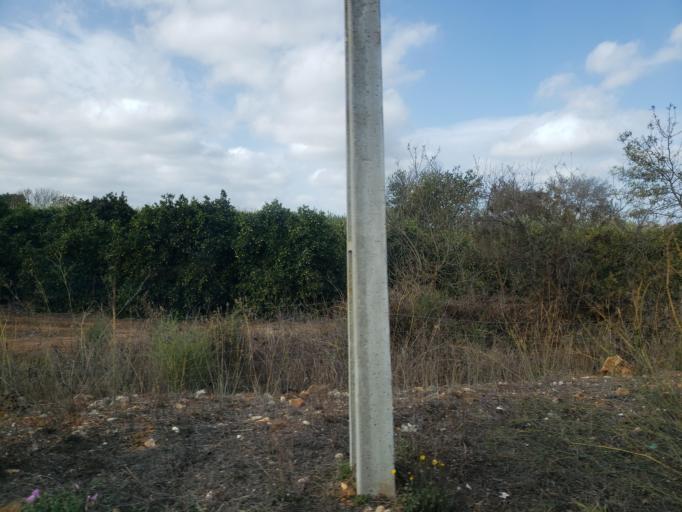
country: PT
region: Faro
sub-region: Portimao
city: Alvor
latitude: 37.1736
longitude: -8.5788
